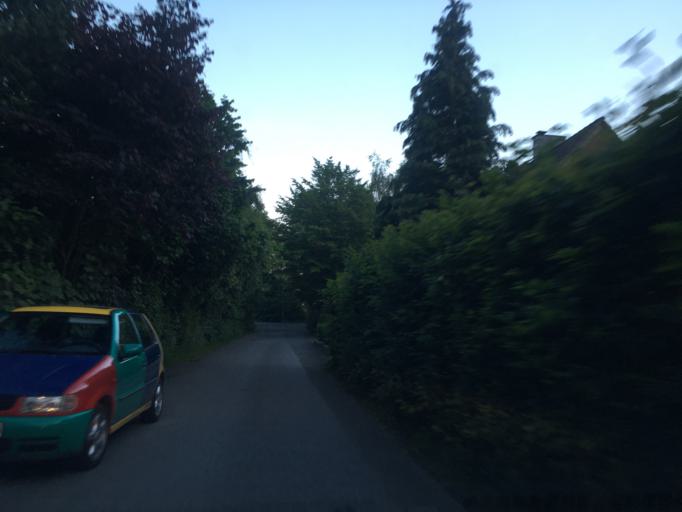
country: DE
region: North Rhine-Westphalia
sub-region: Regierungsbezirk Munster
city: Muenster
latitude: 51.9696
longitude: 7.6670
